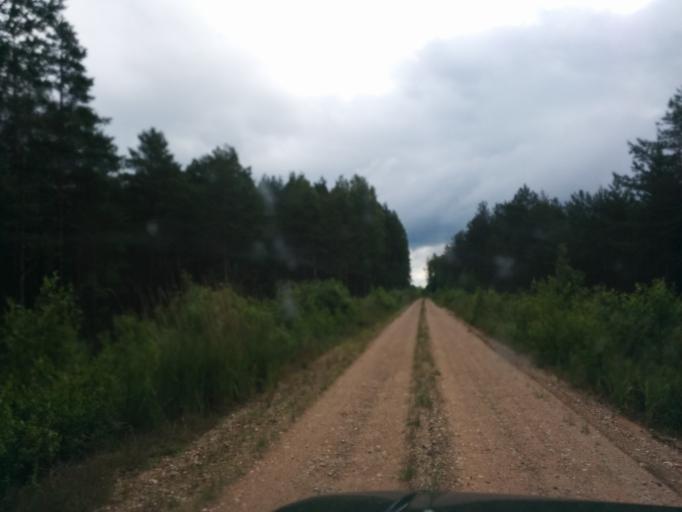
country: LV
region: Vilaka
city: Vilaka
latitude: 57.3930
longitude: 27.6138
